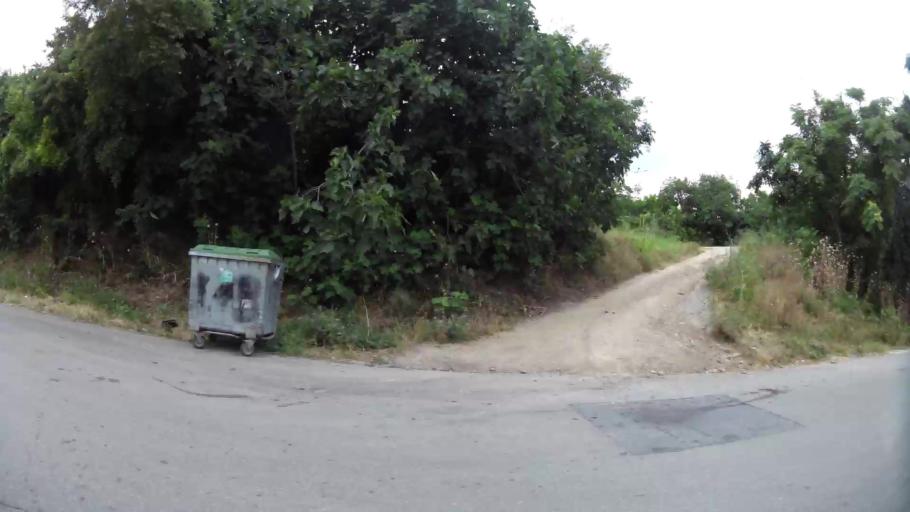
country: GR
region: Central Macedonia
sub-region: Nomos Imathias
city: Veroia
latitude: 40.5227
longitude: 22.2095
